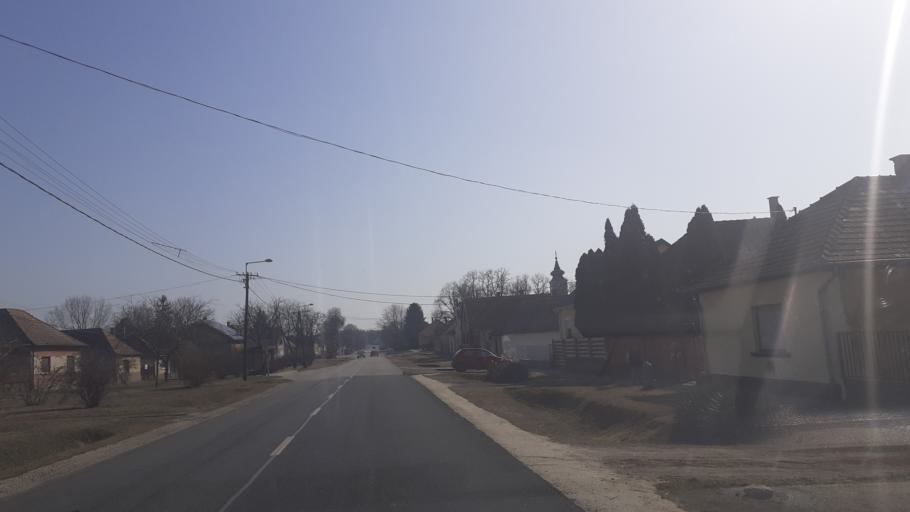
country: HU
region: Pest
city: Orkeny
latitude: 47.0828
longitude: 19.3680
